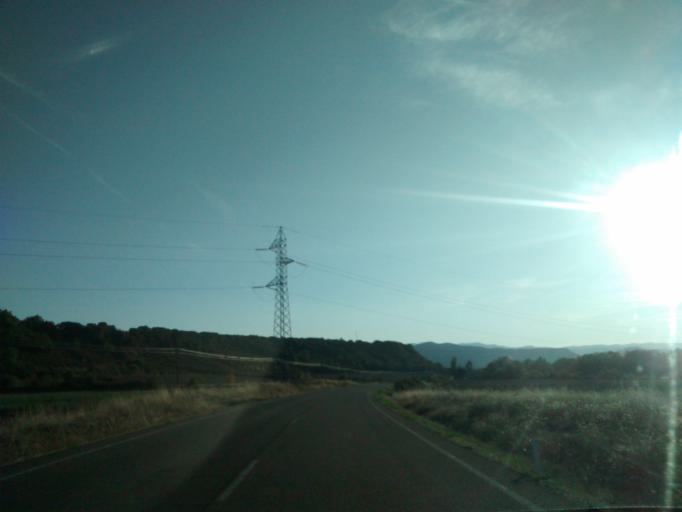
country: ES
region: Aragon
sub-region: Provincia de Huesca
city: Santa Cruz de la Seros
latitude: 42.5802
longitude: -0.7451
